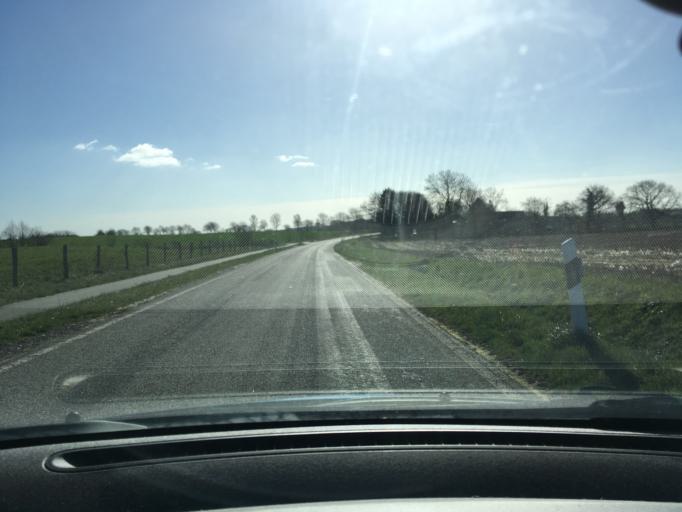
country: DE
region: Schleswig-Holstein
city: Borgwedel
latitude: 54.5007
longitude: 9.6449
